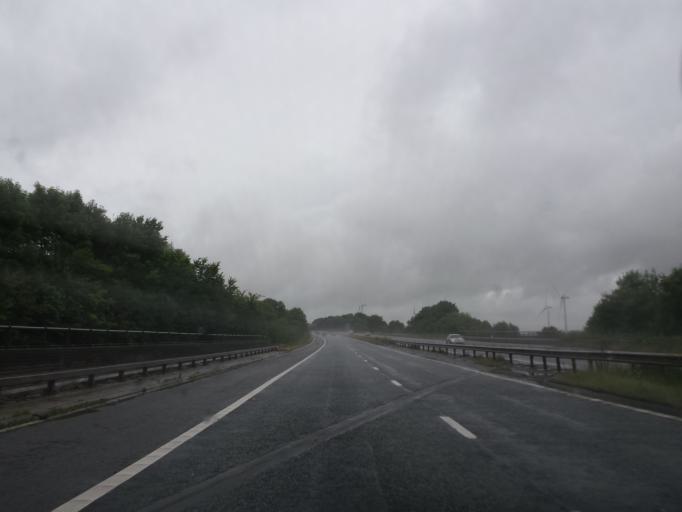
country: GB
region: England
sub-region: Rotherham
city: Bramley
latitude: 53.3963
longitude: -1.2692
